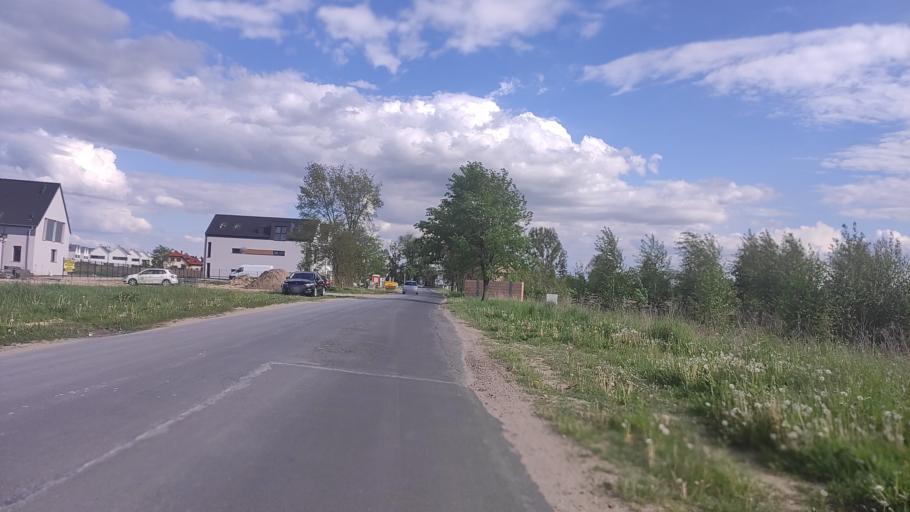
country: PL
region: Greater Poland Voivodeship
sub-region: Powiat poznanski
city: Swarzedz
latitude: 52.3923
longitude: 17.1173
